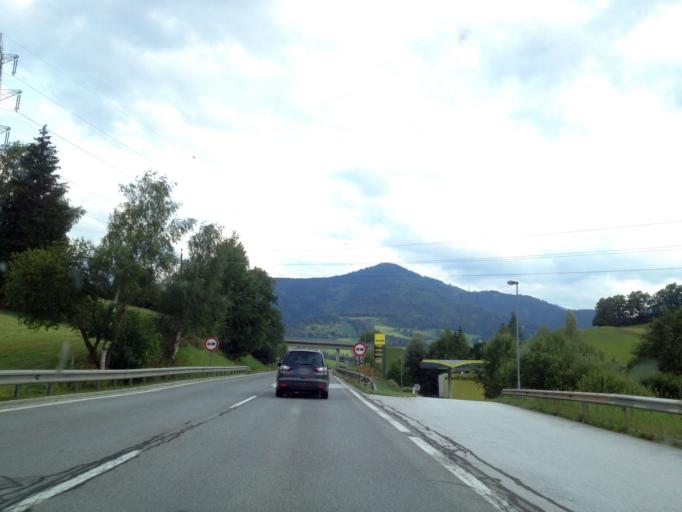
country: AT
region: Styria
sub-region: Politischer Bezirk Liezen
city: Grobming
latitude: 47.4475
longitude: 13.9128
